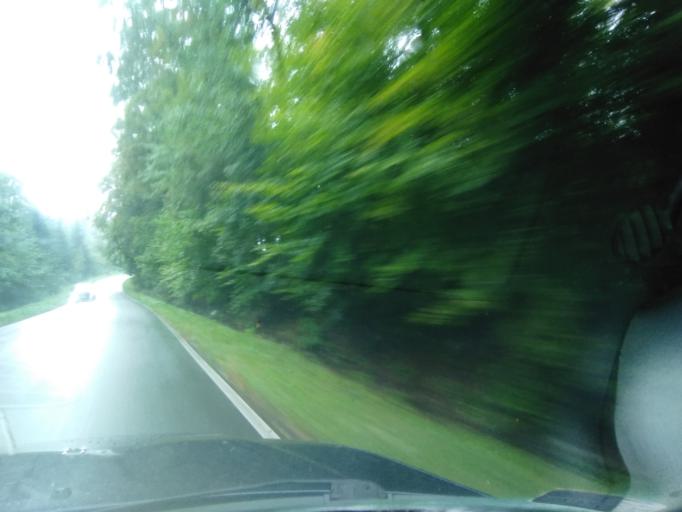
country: PL
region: Subcarpathian Voivodeship
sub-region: Powiat ropczycko-sedziszowski
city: Niedzwiada
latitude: 50.0518
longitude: 21.5345
